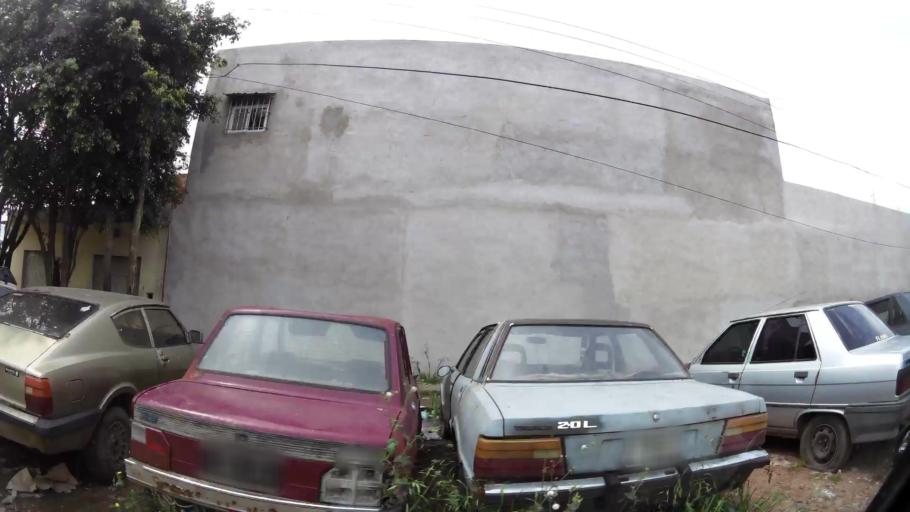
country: AR
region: Buenos Aires
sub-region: Partido de Quilmes
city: Quilmes
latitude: -34.7599
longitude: -58.2625
